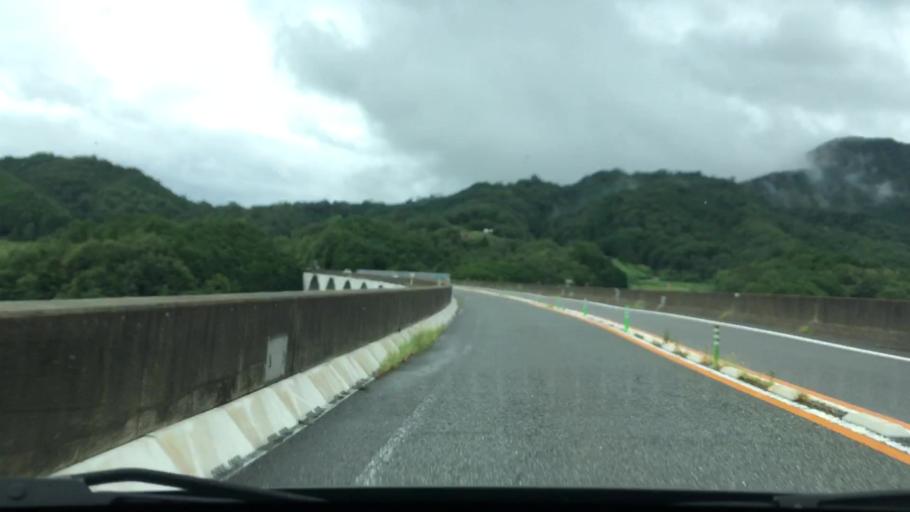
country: JP
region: Hyogo
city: Toyooka
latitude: 35.3103
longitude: 134.8271
